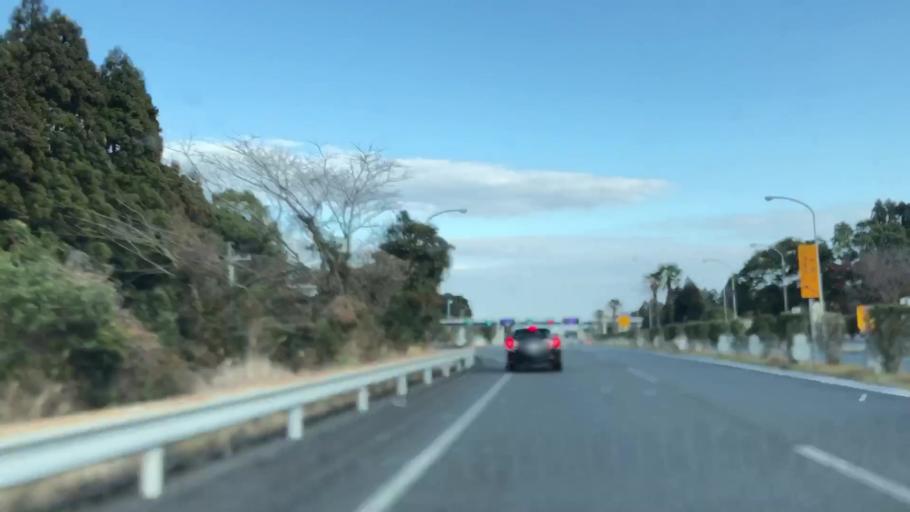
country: JP
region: Miyazaki
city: Miyazaki-shi
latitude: 31.8675
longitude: 131.3960
